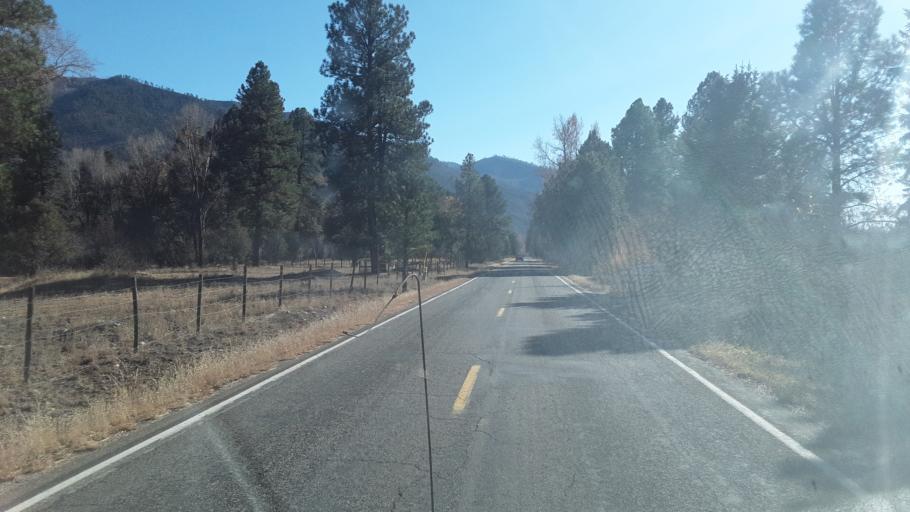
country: US
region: Colorado
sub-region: La Plata County
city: Durango
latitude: 37.4414
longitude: -107.7994
